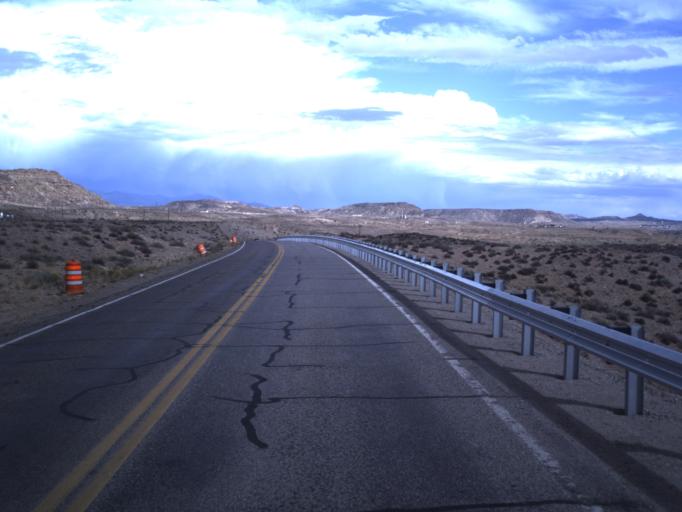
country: US
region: Utah
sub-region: San Juan County
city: Blanding
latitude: 37.2383
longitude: -109.2352
